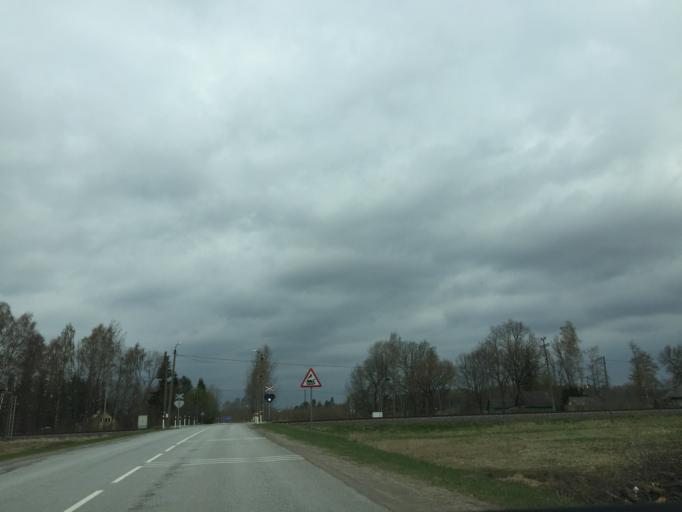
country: EE
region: Tartu
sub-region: Noo vald
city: Noo
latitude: 58.2794
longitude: 26.5282
